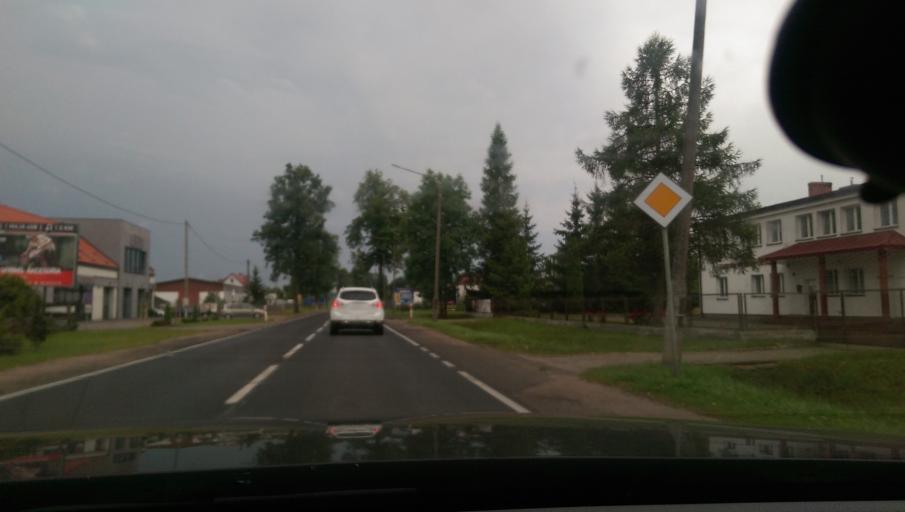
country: PL
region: Warmian-Masurian Voivodeship
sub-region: Powiat szczycienski
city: Szczytno
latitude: 53.5542
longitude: 20.9877
